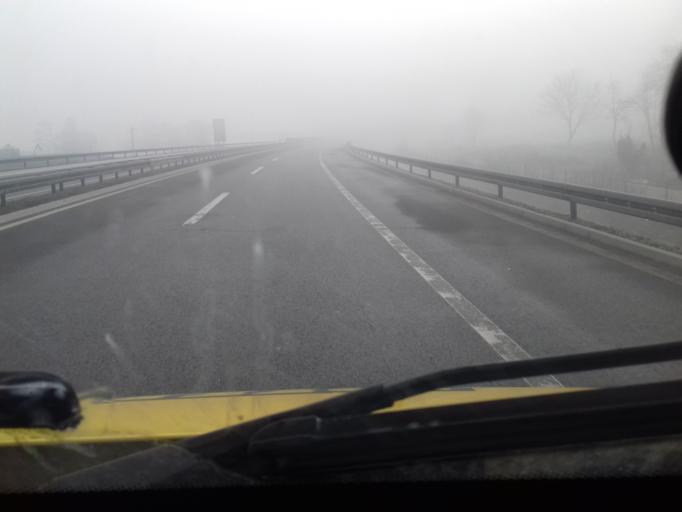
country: BA
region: Federation of Bosnia and Herzegovina
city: Ilijas
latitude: 43.9642
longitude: 18.2575
